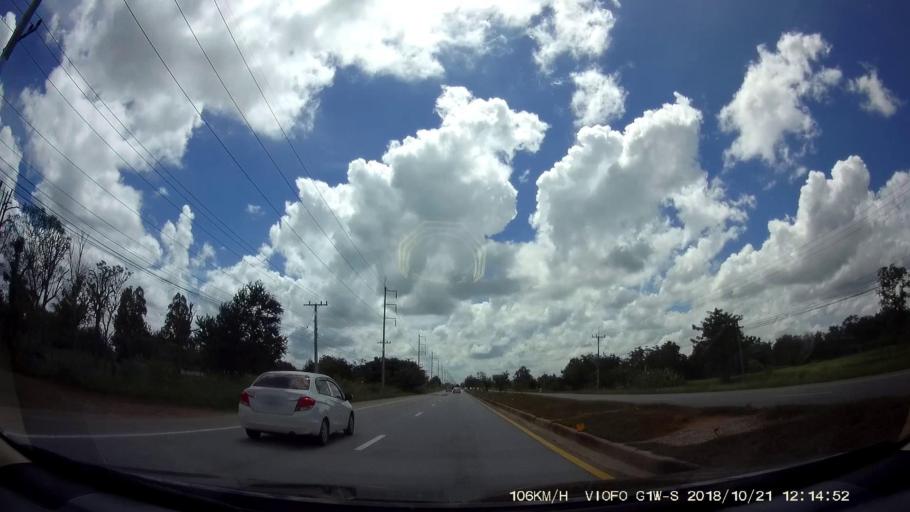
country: TH
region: Nakhon Ratchasima
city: Dan Khun Thot
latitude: 15.3706
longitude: 101.8330
